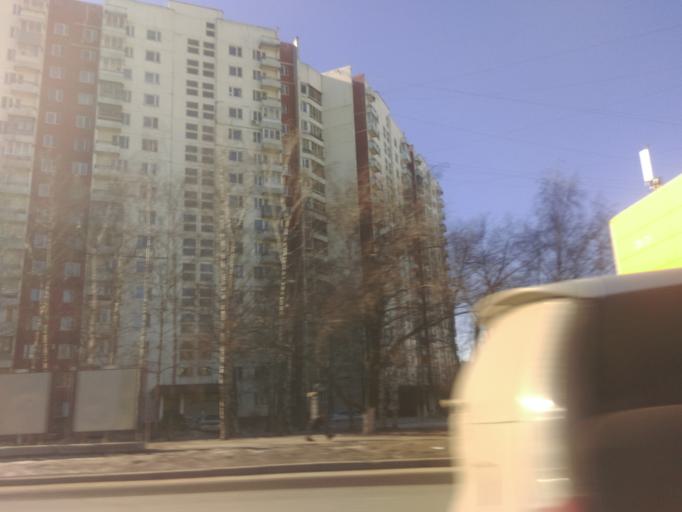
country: RU
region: Moscow
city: Tyoply Stan
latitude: 55.6304
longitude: 37.4829
